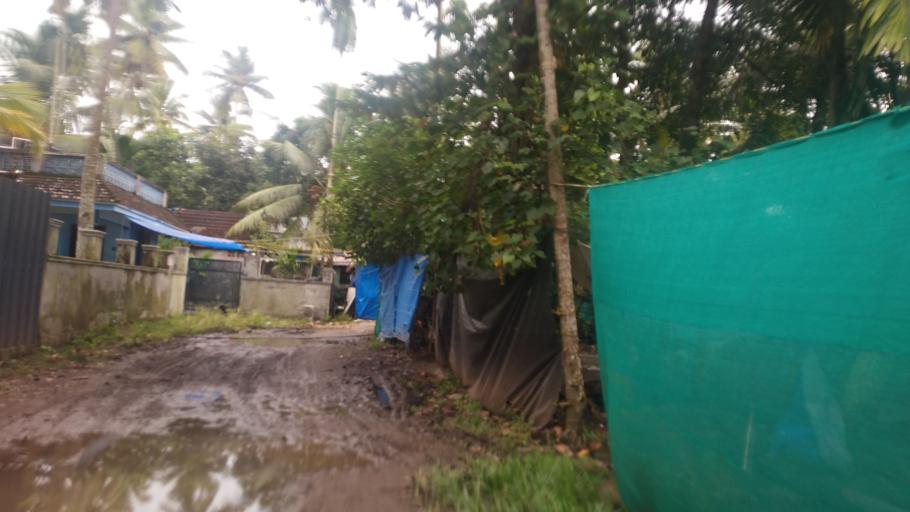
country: IN
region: Kerala
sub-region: Ernakulam
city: Cochin
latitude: 9.8732
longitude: 76.2749
